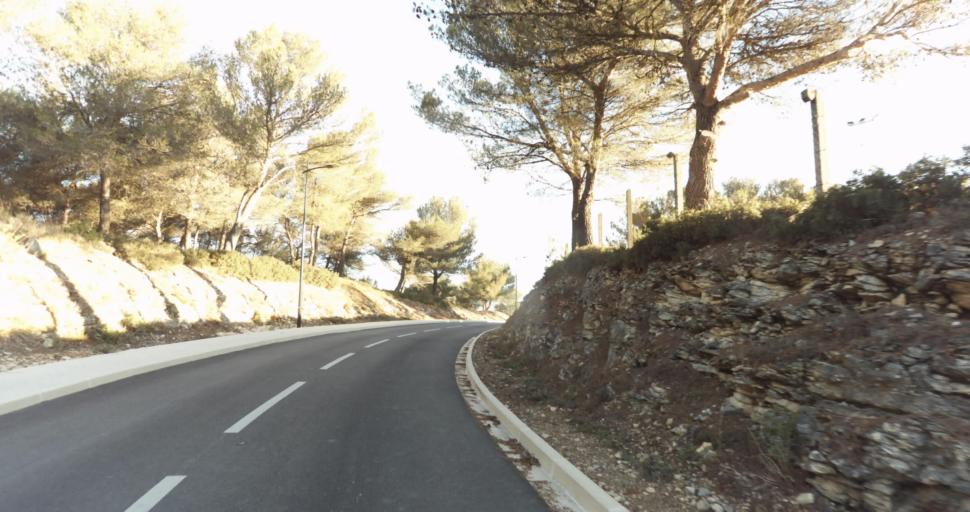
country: FR
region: Provence-Alpes-Cote d'Azur
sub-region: Departement des Bouches-du-Rhone
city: Venelles
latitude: 43.5970
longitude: 5.4923
